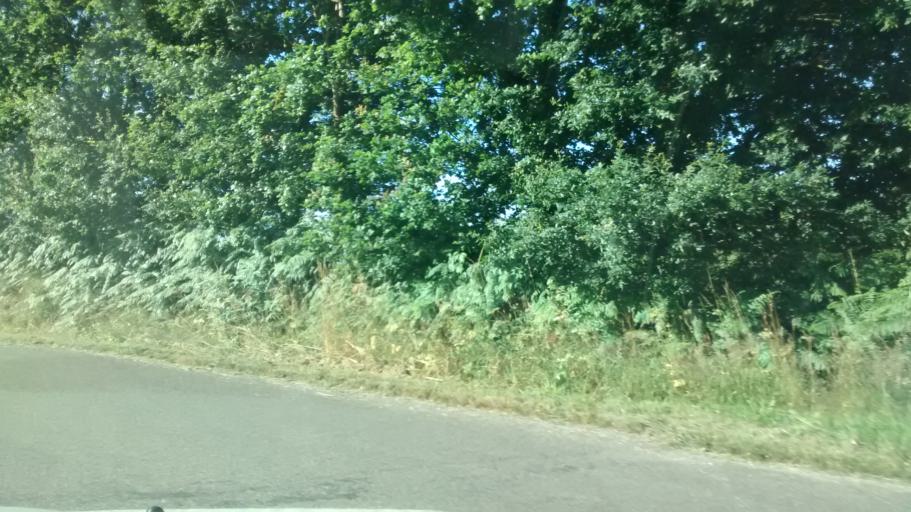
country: FR
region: Brittany
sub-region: Departement du Morbihan
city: Molac
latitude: 47.7875
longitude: -2.4392
